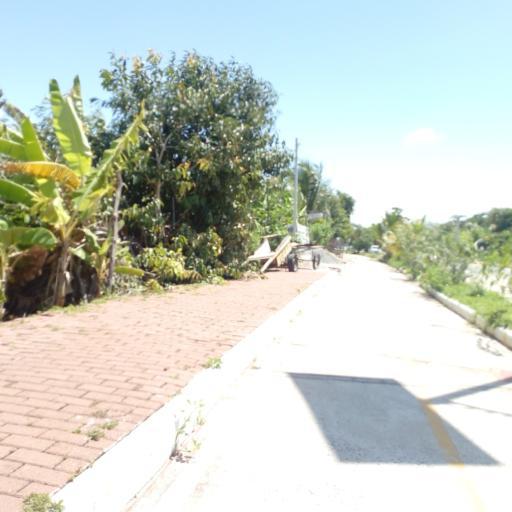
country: BR
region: Pernambuco
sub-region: Ipojuca
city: Ipojuca
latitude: -8.5126
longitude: -35.0097
